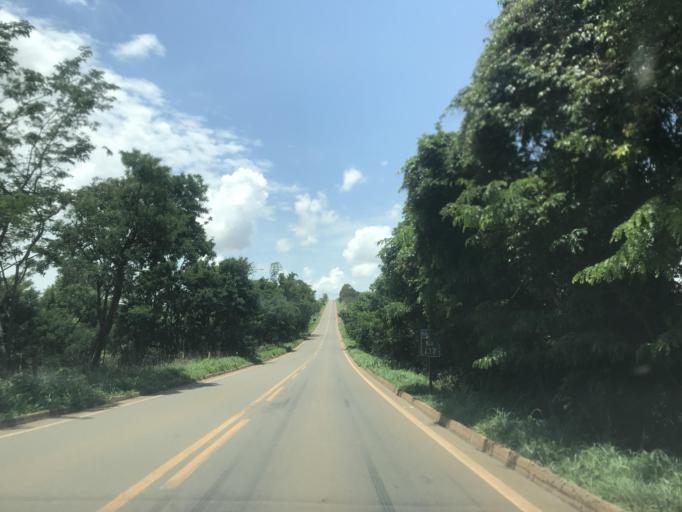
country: BR
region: Goias
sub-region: Luziania
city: Luziania
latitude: -16.4826
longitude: -48.2037
